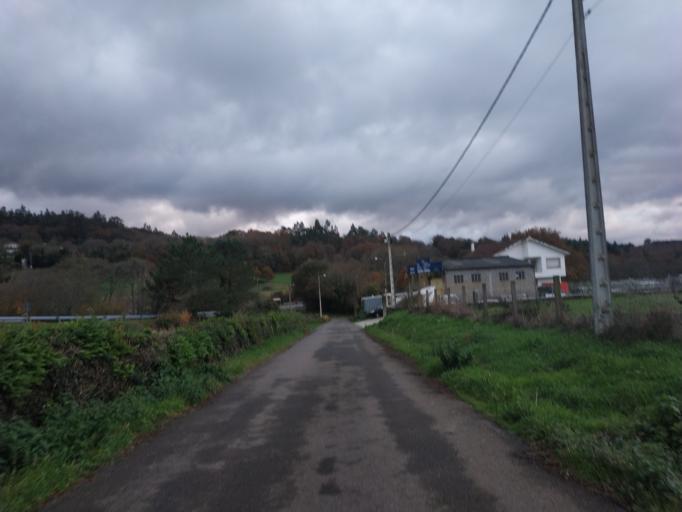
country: ES
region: Galicia
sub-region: Provincia de Pontevedra
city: Silleda
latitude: 42.7822
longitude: -8.1717
